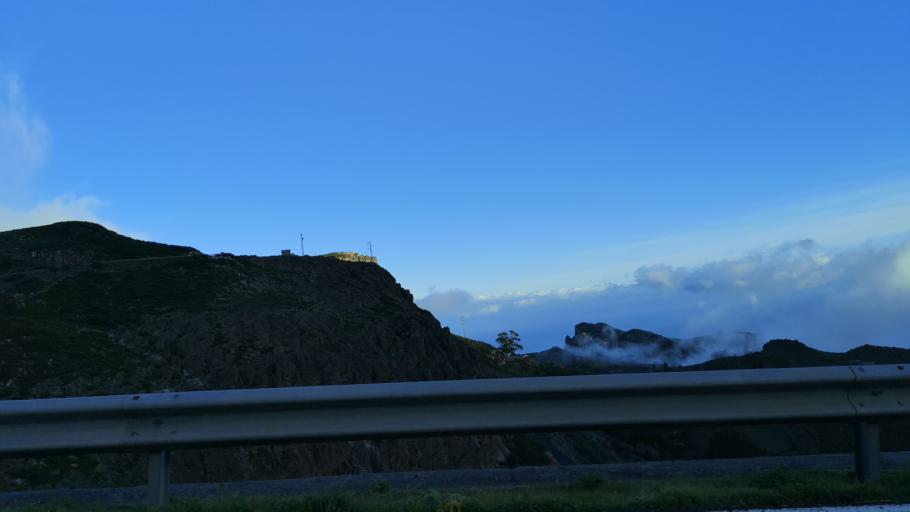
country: ES
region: Canary Islands
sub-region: Provincia de Santa Cruz de Tenerife
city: Alajero
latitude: 28.0900
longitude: -17.2540
